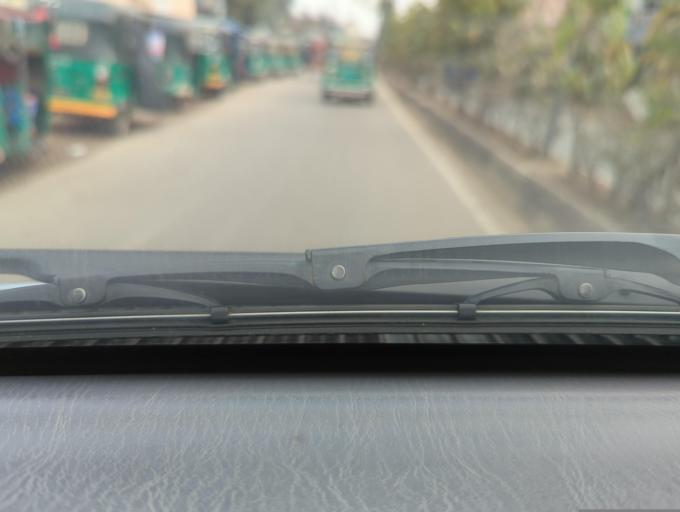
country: BD
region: Sylhet
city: Maulavi Bazar
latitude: 24.4900
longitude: 91.7559
